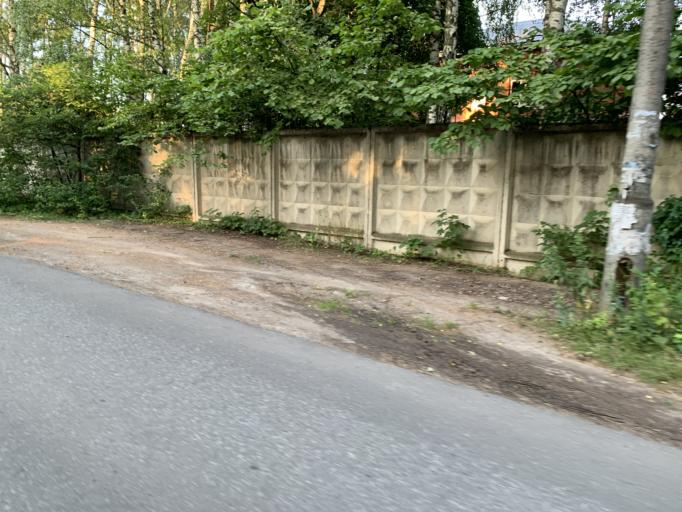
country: RU
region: Moskovskaya
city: Lesnyye Polyany
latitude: 55.9747
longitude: 37.8462
